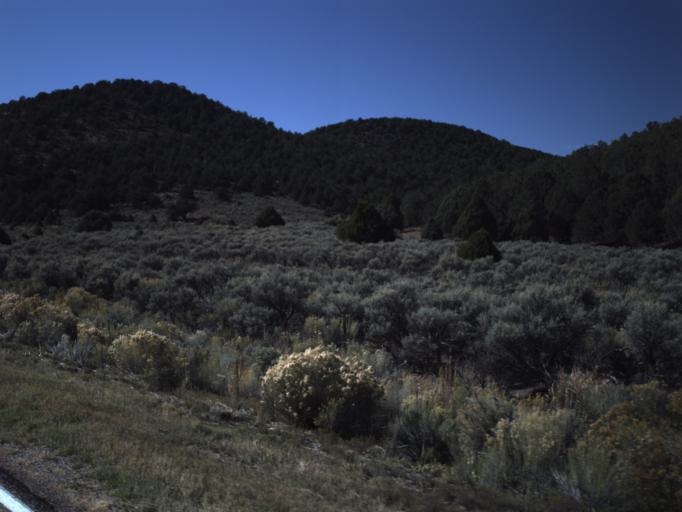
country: US
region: Utah
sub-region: Garfield County
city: Panguitch
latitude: 37.7651
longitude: -112.4952
